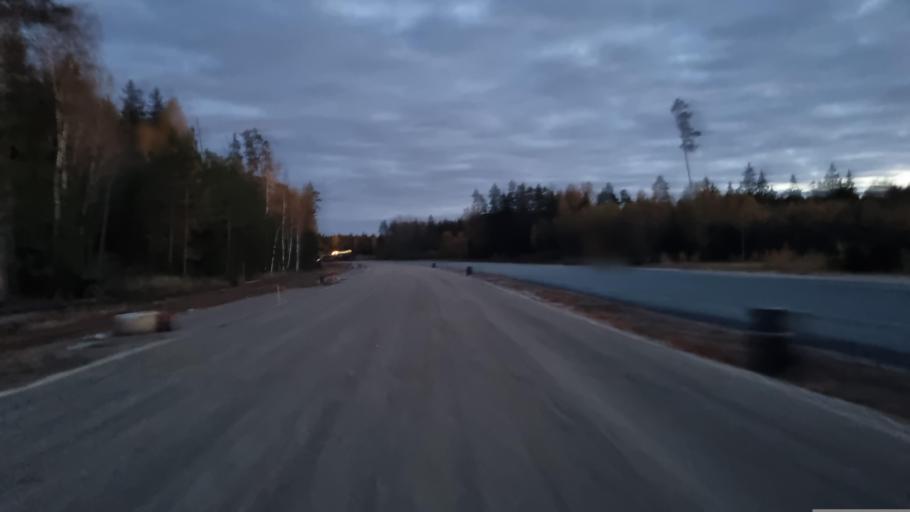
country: LV
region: Kekava
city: Balozi
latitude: 56.8322
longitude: 24.1573
